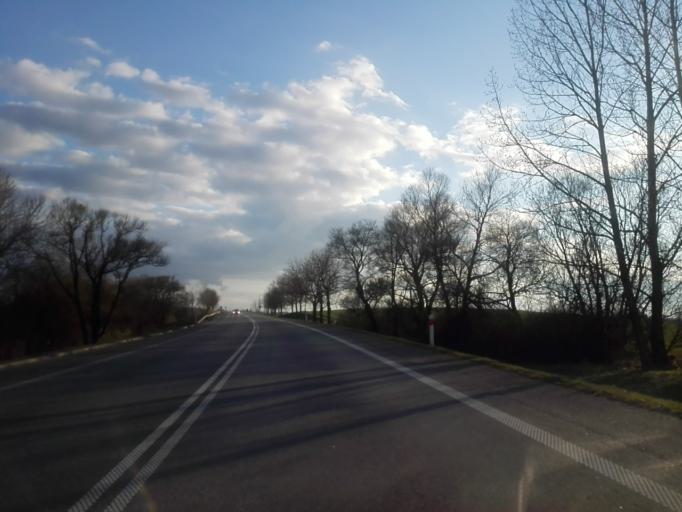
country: PL
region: Podlasie
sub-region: Suwalki
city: Suwalki
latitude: 54.1880
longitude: 23.0059
